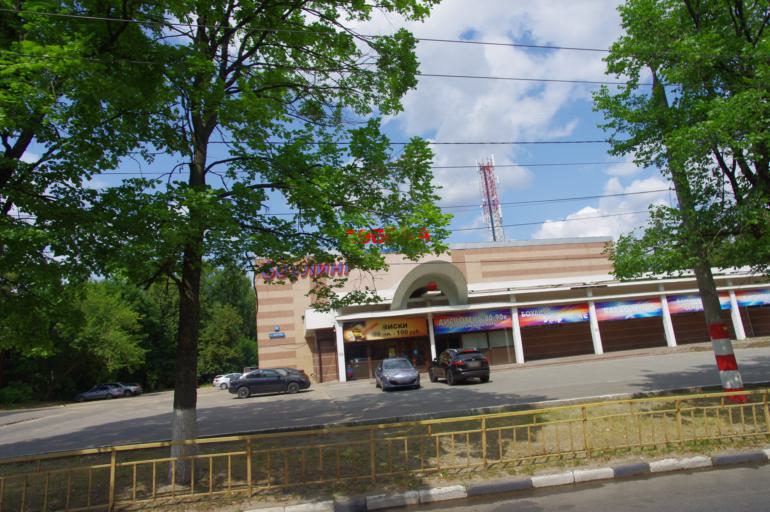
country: RU
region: Nizjnij Novgorod
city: Nizhniy Novgorod
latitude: 56.2920
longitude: 44.0049
